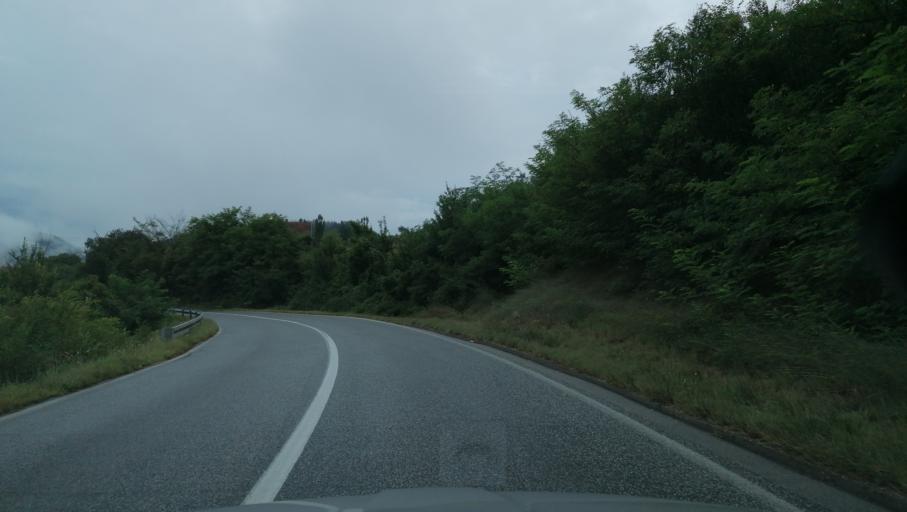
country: BA
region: Republika Srpska
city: Visegrad
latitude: 43.7842
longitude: 19.3138
